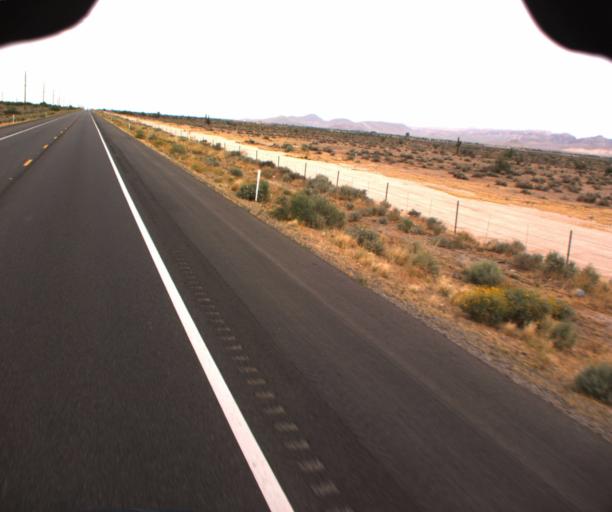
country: US
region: Arizona
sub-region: Pinal County
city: Blackwater
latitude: 33.0380
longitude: -111.6579
